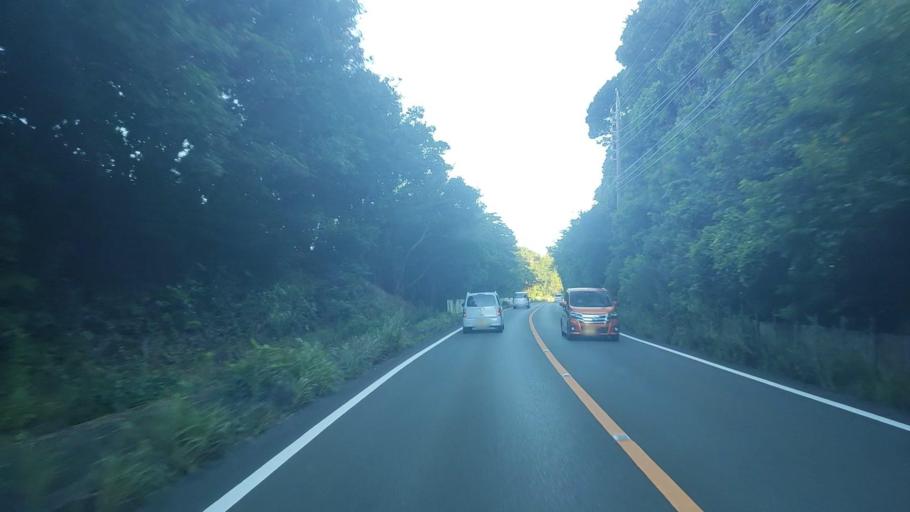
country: JP
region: Mie
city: Toba
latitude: 34.2660
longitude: 136.8683
